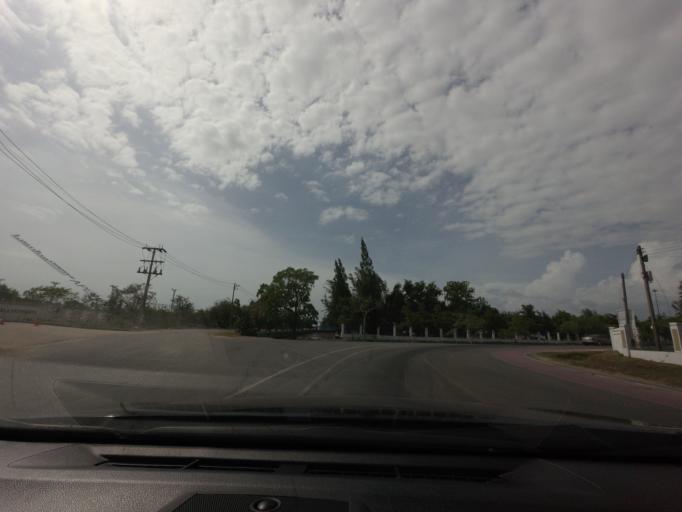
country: TH
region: Pattani
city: Pattani
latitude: 6.8883
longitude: 101.2422
